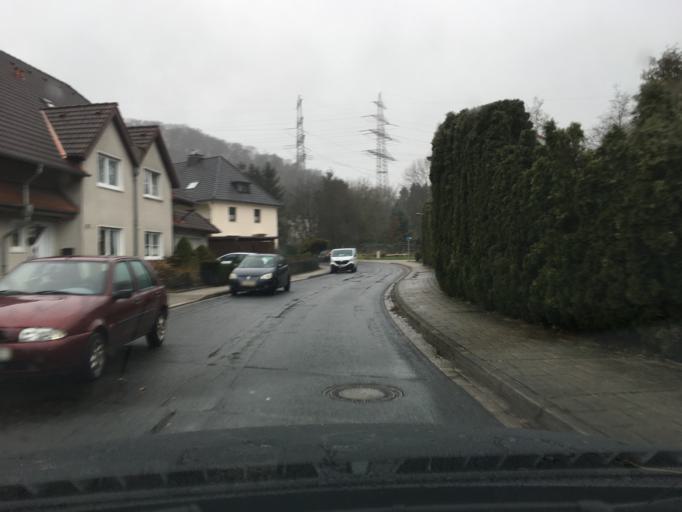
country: DE
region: North Rhine-Westphalia
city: Hattingen
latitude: 51.3862
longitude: 7.1713
